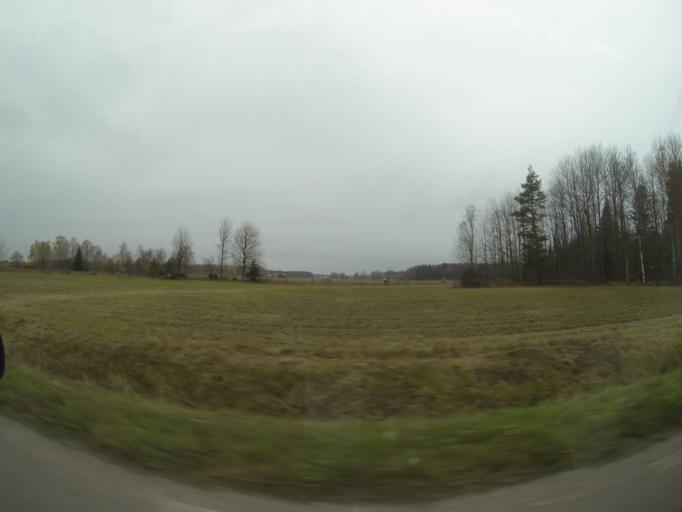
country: SE
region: Vaestmanland
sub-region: Kopings Kommun
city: Koping
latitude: 59.5800
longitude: 16.0836
